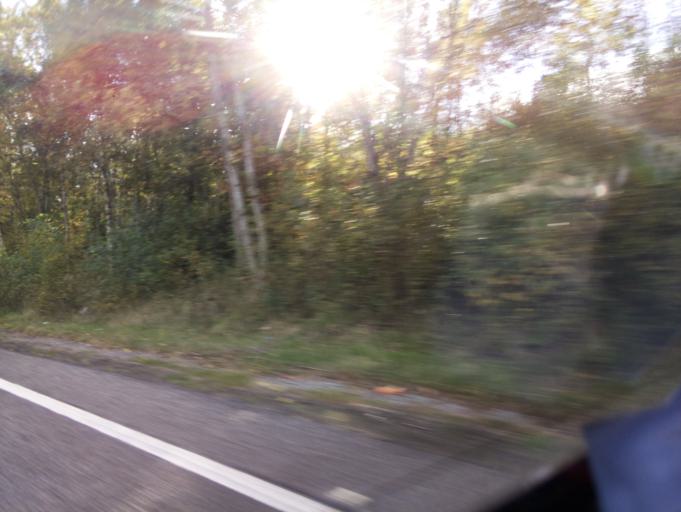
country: GB
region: Wales
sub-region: Merthyr Tydfil County Borough
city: Abercanaid
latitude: 51.7280
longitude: -3.3764
